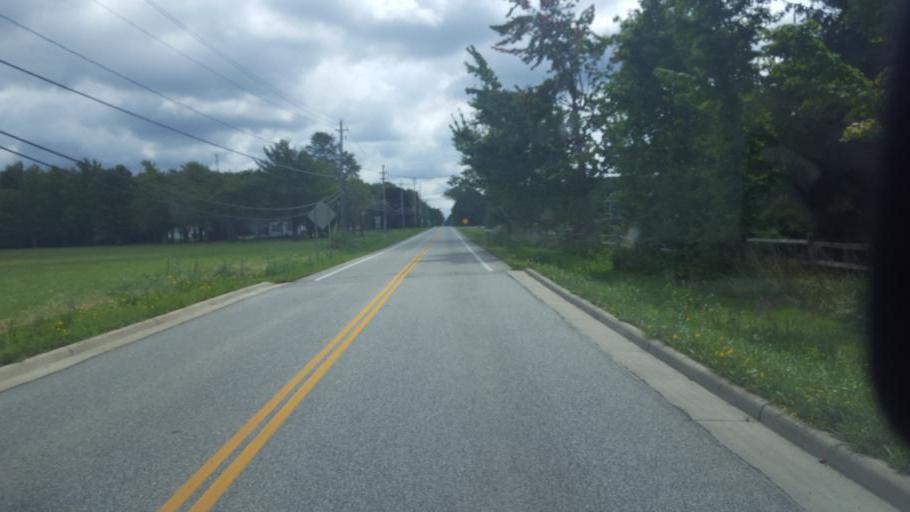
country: US
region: Ohio
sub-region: Geauga County
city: Chardon
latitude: 41.6861
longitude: -81.1749
